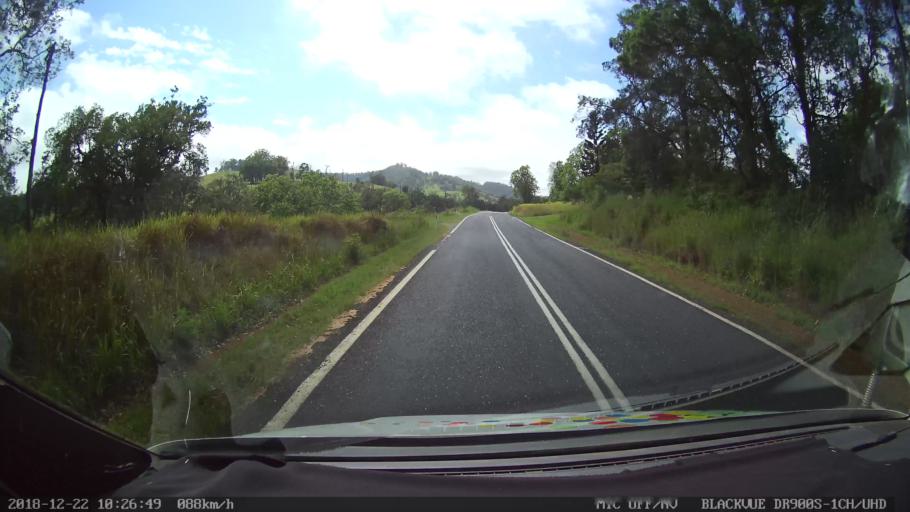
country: AU
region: New South Wales
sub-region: Clarence Valley
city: Gordon
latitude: -29.5911
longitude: 152.5747
